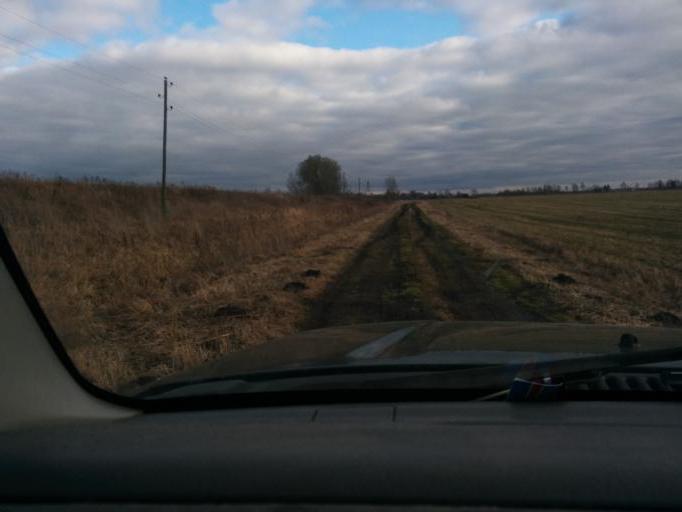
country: LV
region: Jelgava
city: Jelgava
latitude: 56.6901
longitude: 23.6877
